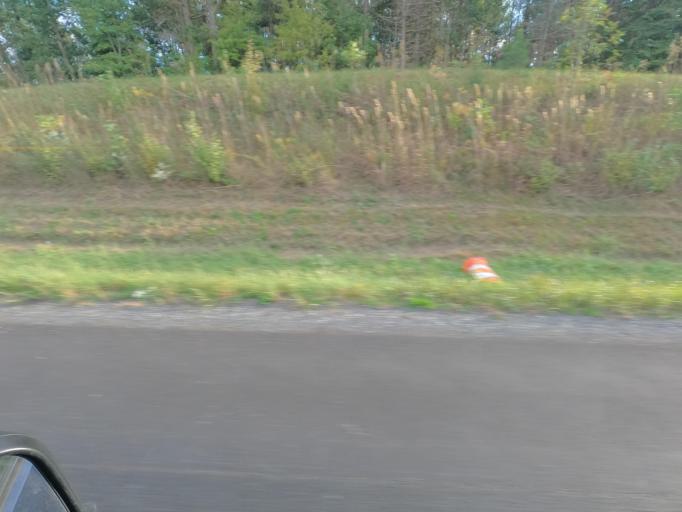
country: US
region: Tennessee
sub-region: Decatur County
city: Parsons
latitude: 35.8194
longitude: -88.1735
